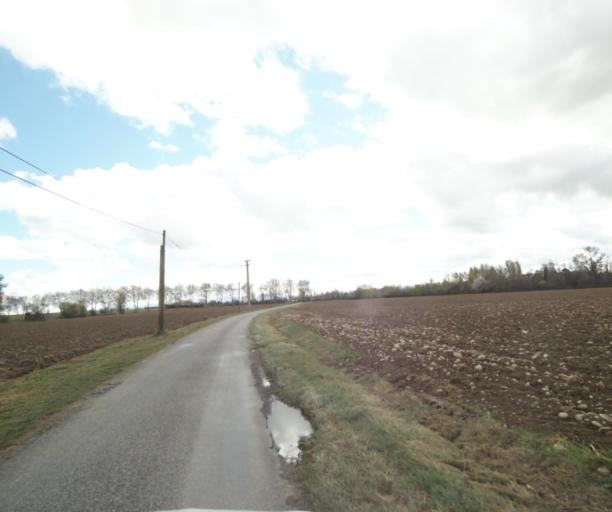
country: FR
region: Midi-Pyrenees
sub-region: Departement de l'Ariege
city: Saverdun
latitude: 43.2575
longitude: 1.5820
